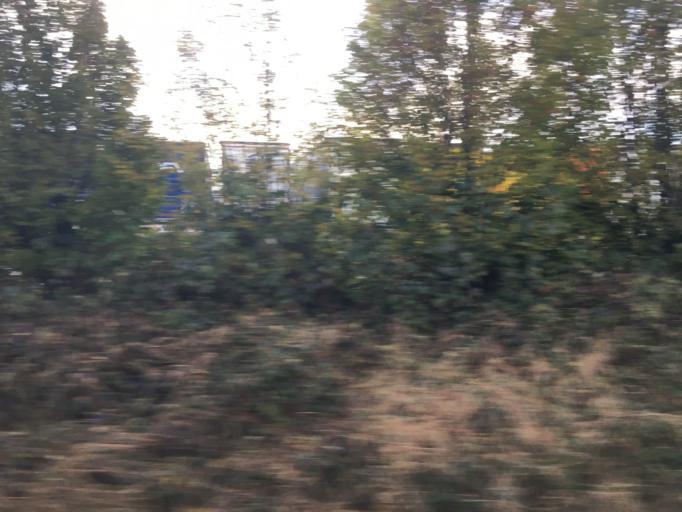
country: DE
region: North Rhine-Westphalia
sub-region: Regierungsbezirk Munster
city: Nordwalde
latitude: 52.0765
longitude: 7.4623
